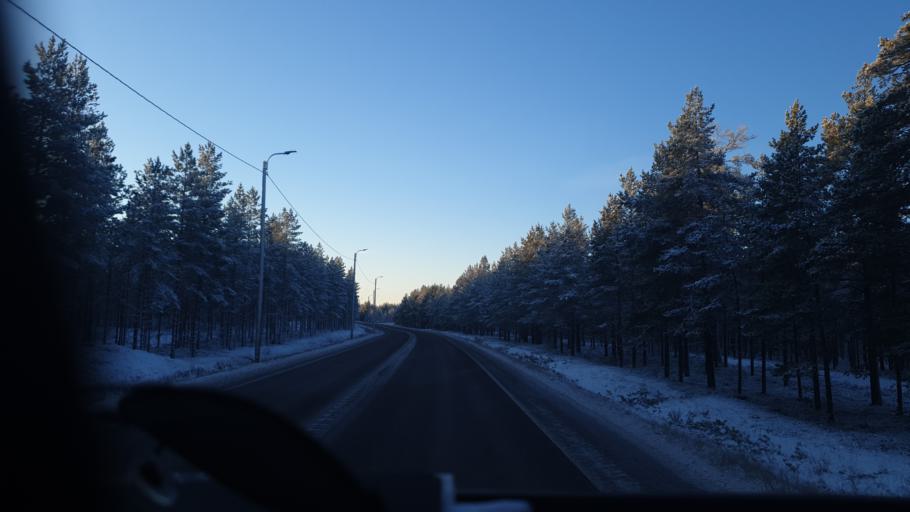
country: FI
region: Northern Ostrobothnia
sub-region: Ylivieska
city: Kalajoki
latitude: 64.2387
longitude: 23.8377
